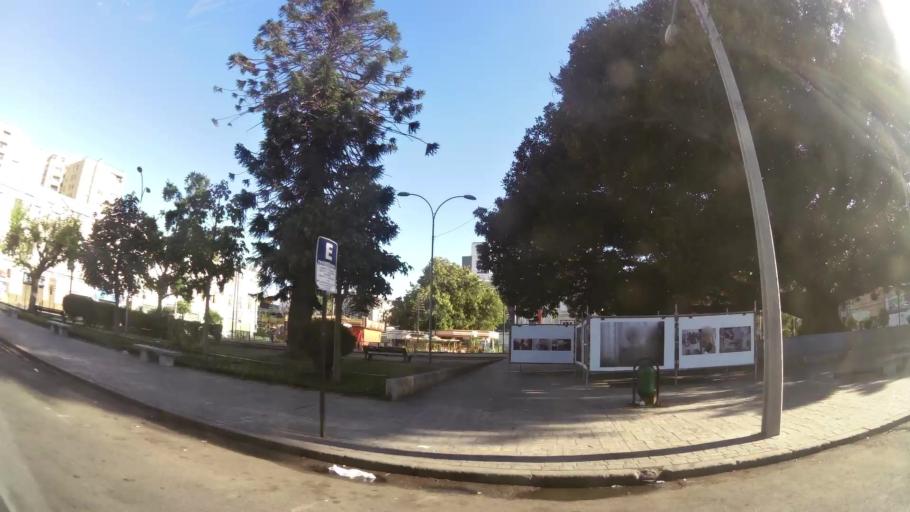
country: CL
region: Valparaiso
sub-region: Provincia de Valparaiso
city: Valparaiso
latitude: -33.0459
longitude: -71.6196
